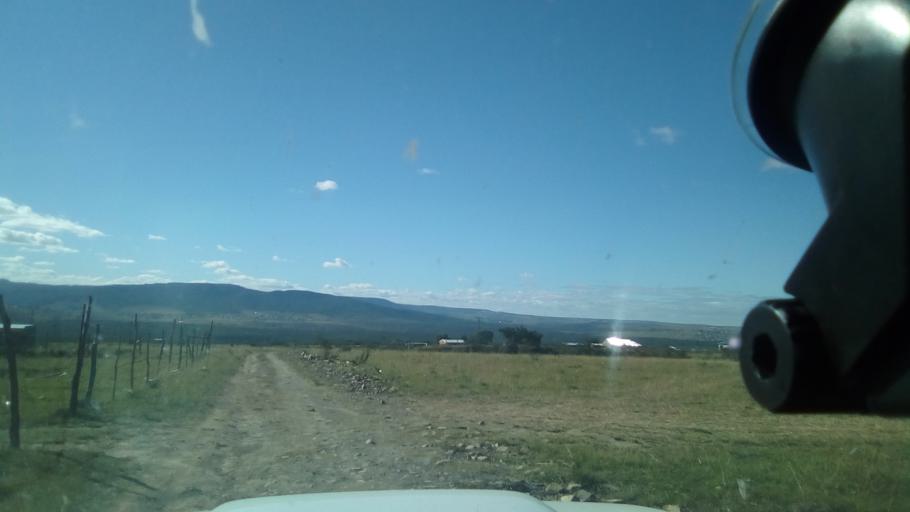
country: ZA
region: Eastern Cape
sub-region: Buffalo City Metropolitan Municipality
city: Bhisho
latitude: -32.7809
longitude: 27.3342
